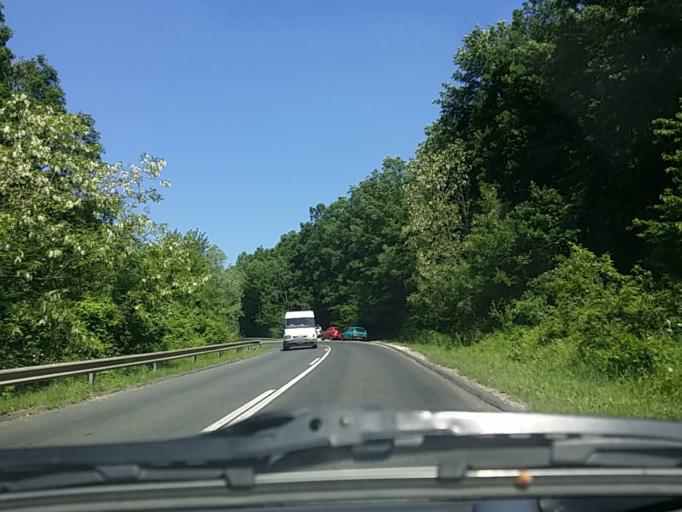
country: HU
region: Pest
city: Pilisszentkereszt
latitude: 47.6897
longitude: 18.9127
